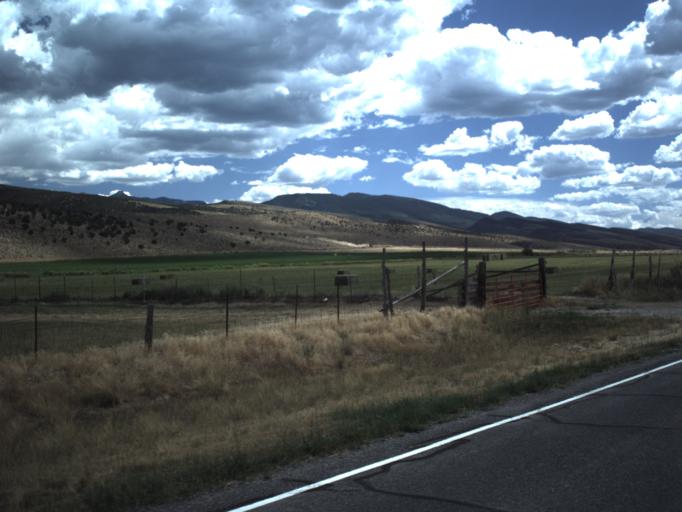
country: US
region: Utah
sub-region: Sanpete County
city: Gunnison
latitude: 39.1595
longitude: -111.7076
